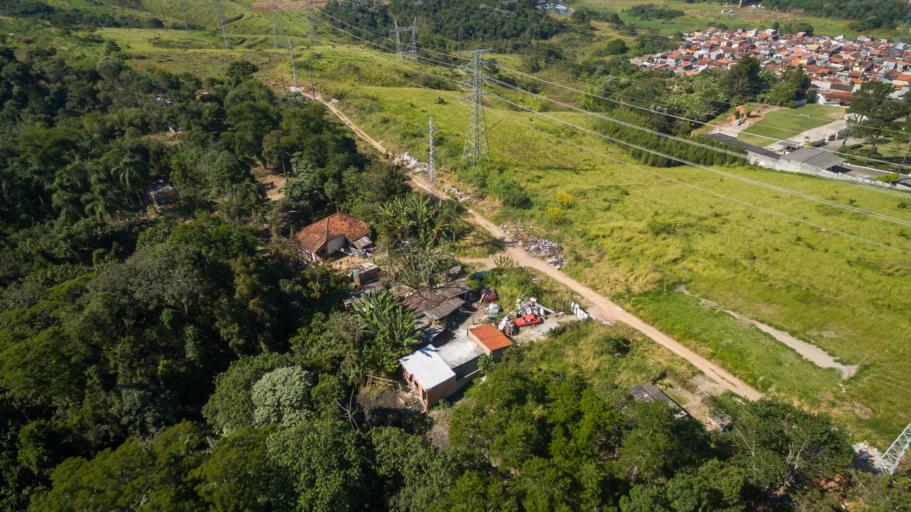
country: BR
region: Sao Paulo
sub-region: Mogi das Cruzes
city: Mogi das Cruzes
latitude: -23.5372
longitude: -46.1666
